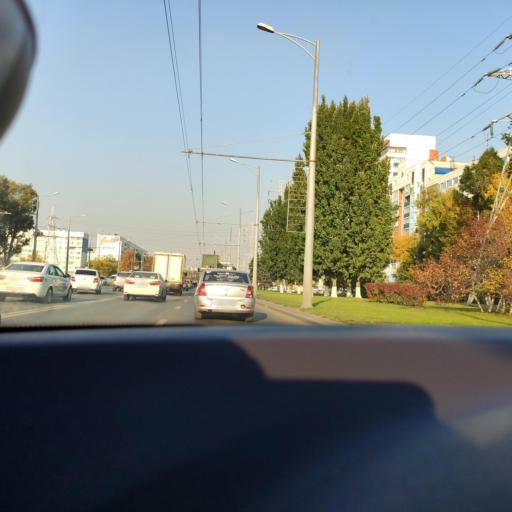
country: RU
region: Samara
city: Samara
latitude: 53.2412
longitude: 50.2078
